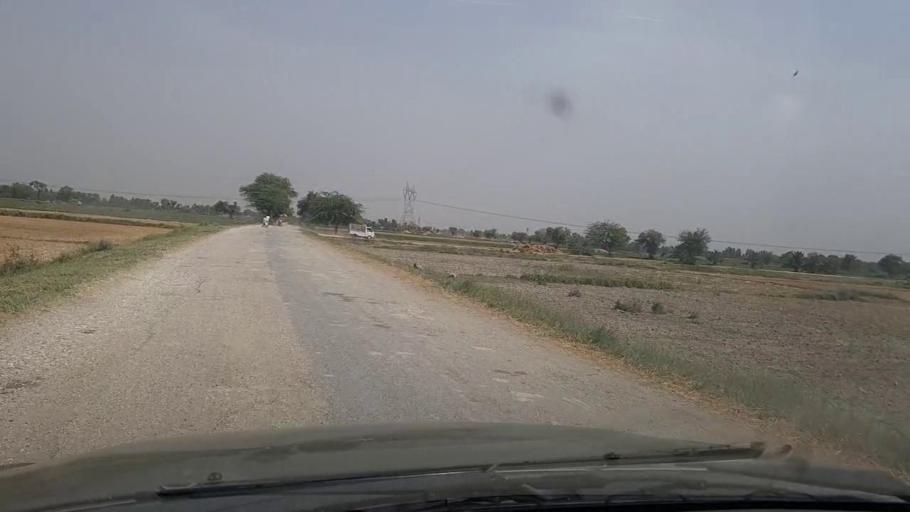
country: PK
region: Sindh
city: Shikarpur
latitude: 27.9220
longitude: 68.6745
